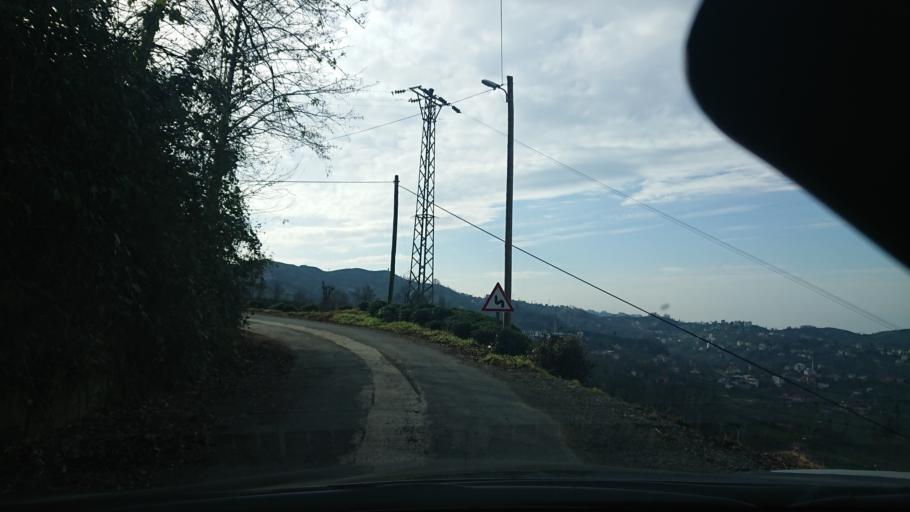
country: TR
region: Rize
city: Rize
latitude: 40.9863
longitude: 40.4921
